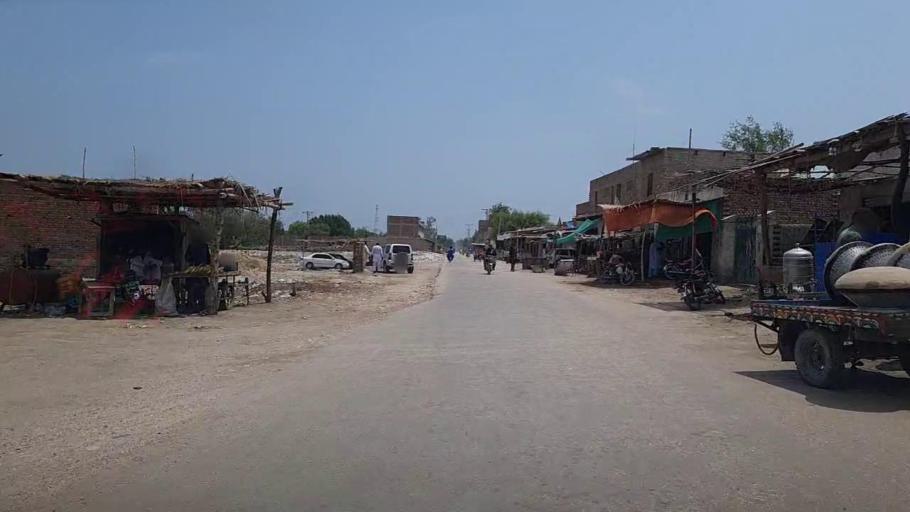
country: PK
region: Sindh
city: Khairpur
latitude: 28.0535
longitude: 69.6904
